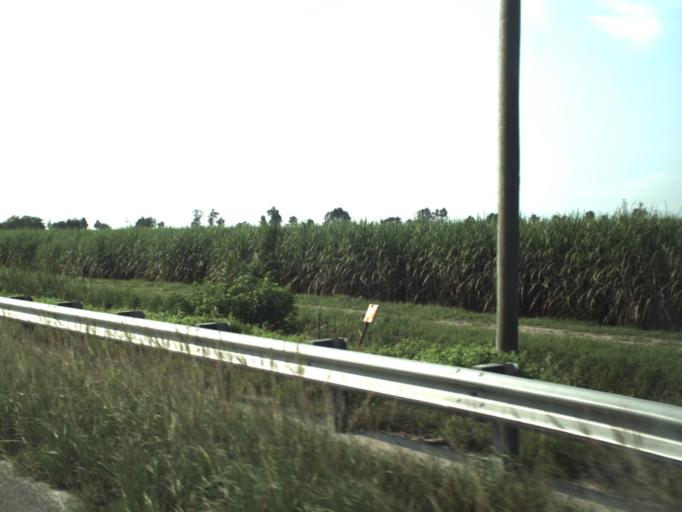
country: US
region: Florida
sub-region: Hendry County
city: Clewiston
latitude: 26.7349
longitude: -80.8676
